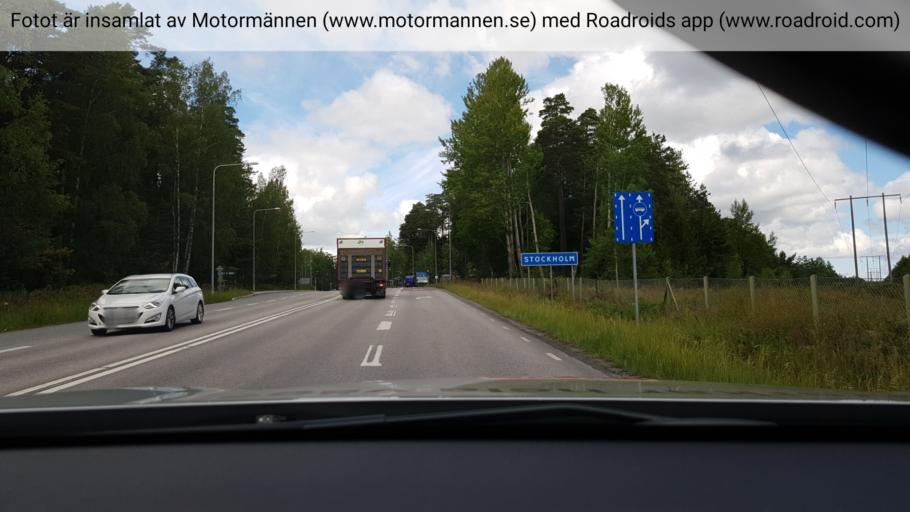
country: SE
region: Stockholm
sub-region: Tyreso Kommun
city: Bollmora
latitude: 59.2324
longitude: 18.1944
